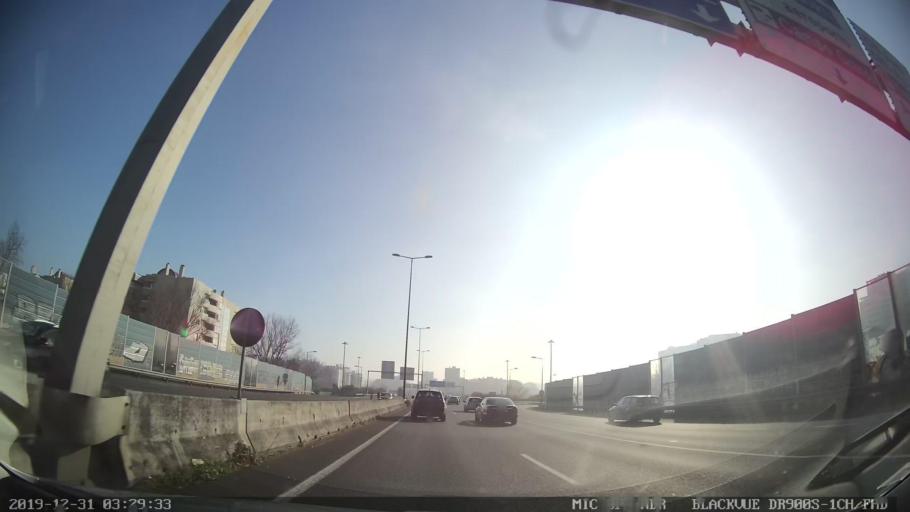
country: PT
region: Lisbon
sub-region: Odivelas
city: Pontinha
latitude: 38.7593
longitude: -9.1730
